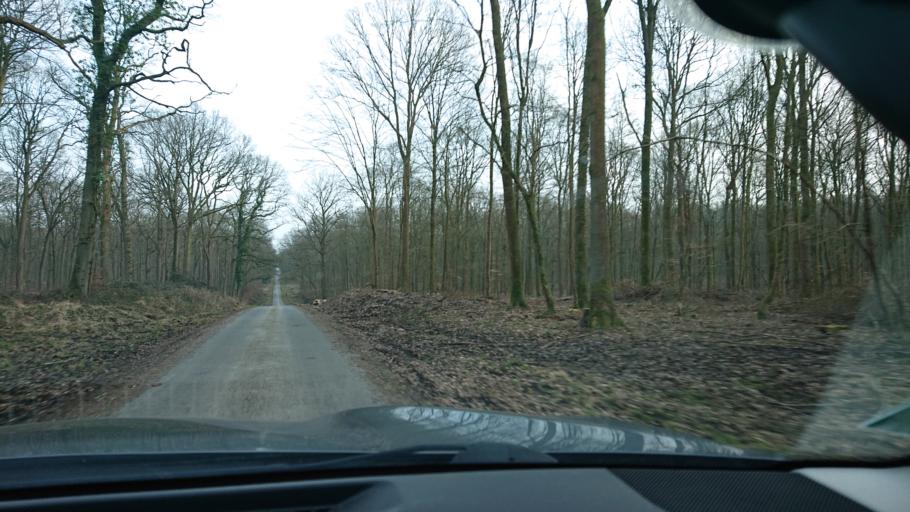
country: FR
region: Nord-Pas-de-Calais
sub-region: Departement du Nord
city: Landrecies
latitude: 50.1635
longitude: 3.7085
